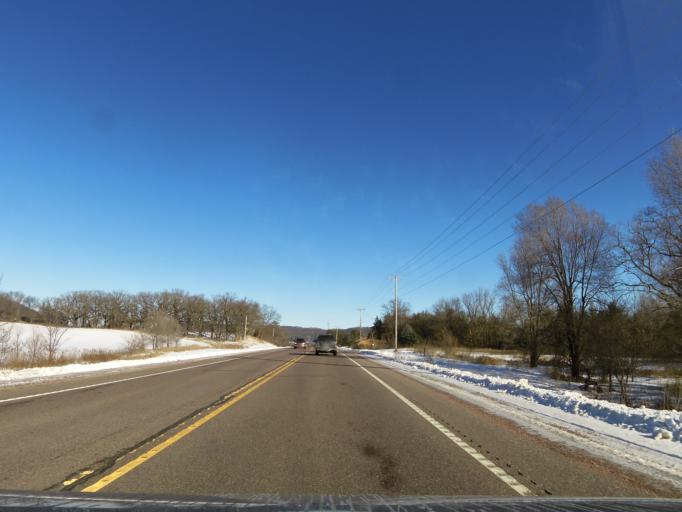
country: US
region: Wisconsin
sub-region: Sauk County
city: Baraboo
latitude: 43.4782
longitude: -89.6472
